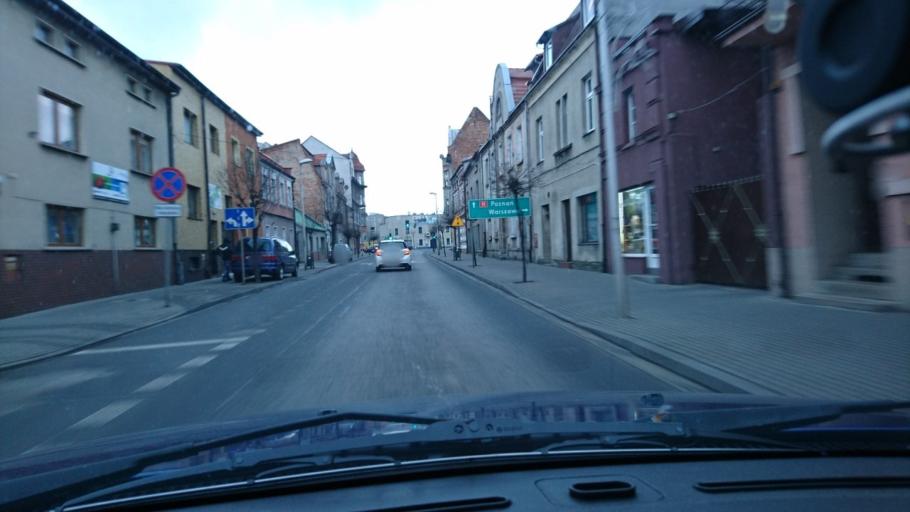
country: PL
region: Greater Poland Voivodeship
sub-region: Powiat kepinski
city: Kepno
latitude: 51.2838
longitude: 17.9926
